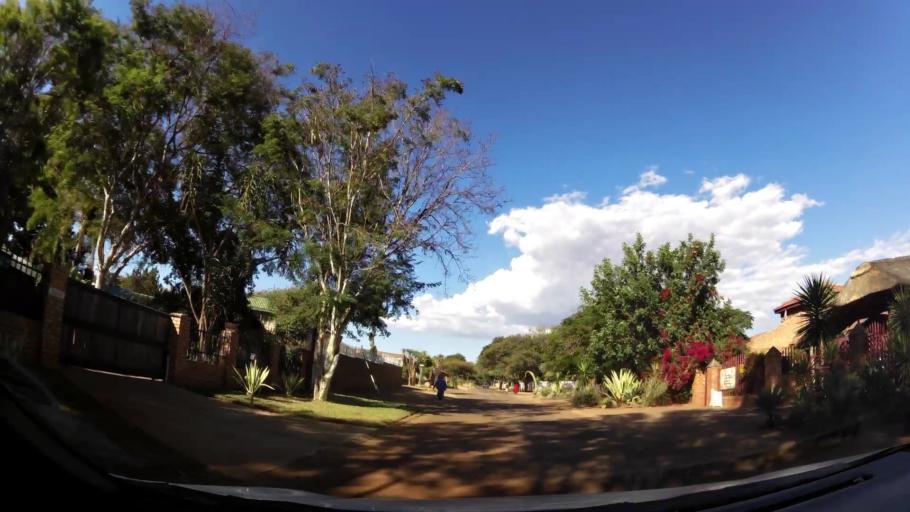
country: ZA
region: Limpopo
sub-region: Waterberg District Municipality
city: Mokopane
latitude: -24.2078
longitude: 28.9920
